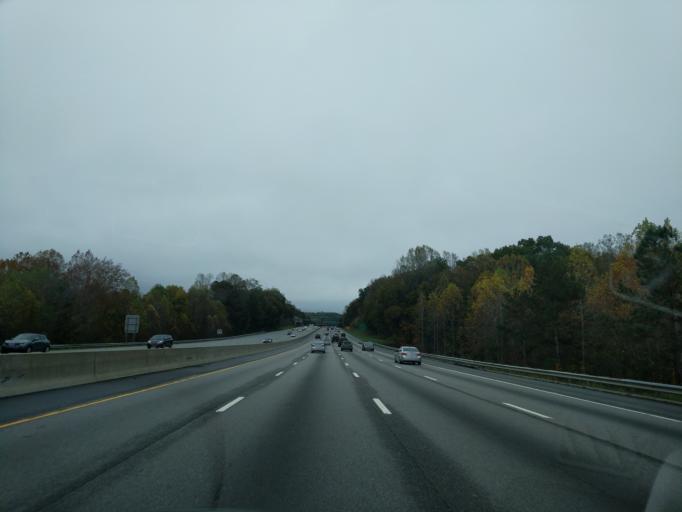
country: US
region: North Carolina
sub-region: Orange County
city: Hillsborough
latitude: 36.0668
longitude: -79.1461
